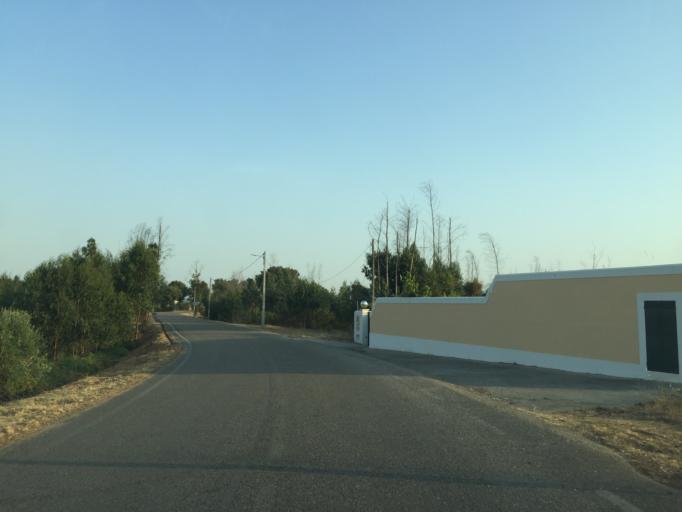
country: PT
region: Santarem
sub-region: Tomar
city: Tomar
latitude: 39.5800
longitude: -8.2977
